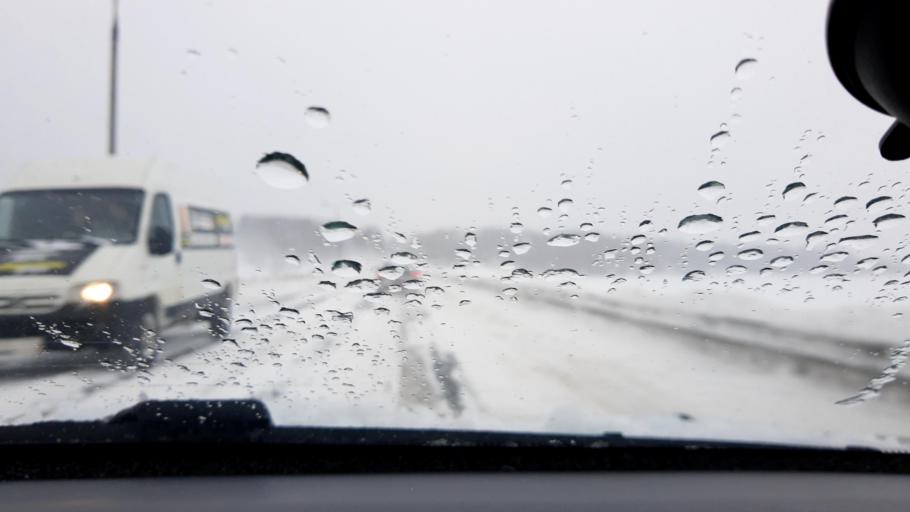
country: RU
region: Nizjnij Novgorod
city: Pervomayskiy
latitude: 56.6380
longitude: 43.2593
